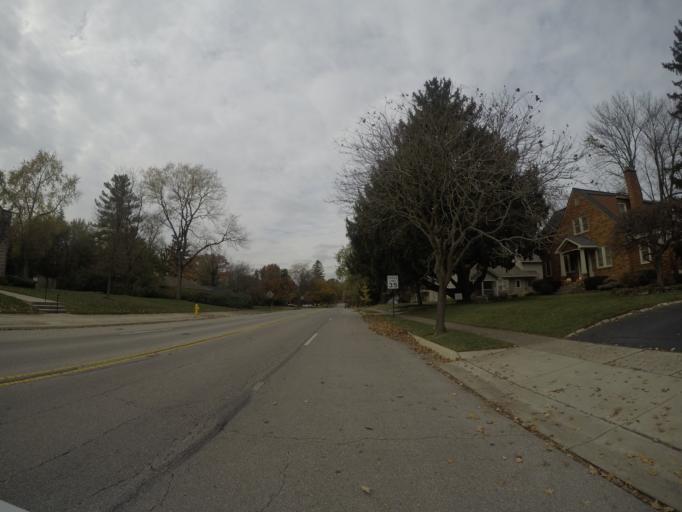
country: US
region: Ohio
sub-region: Franklin County
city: Upper Arlington
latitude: 40.0197
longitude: -83.0854
